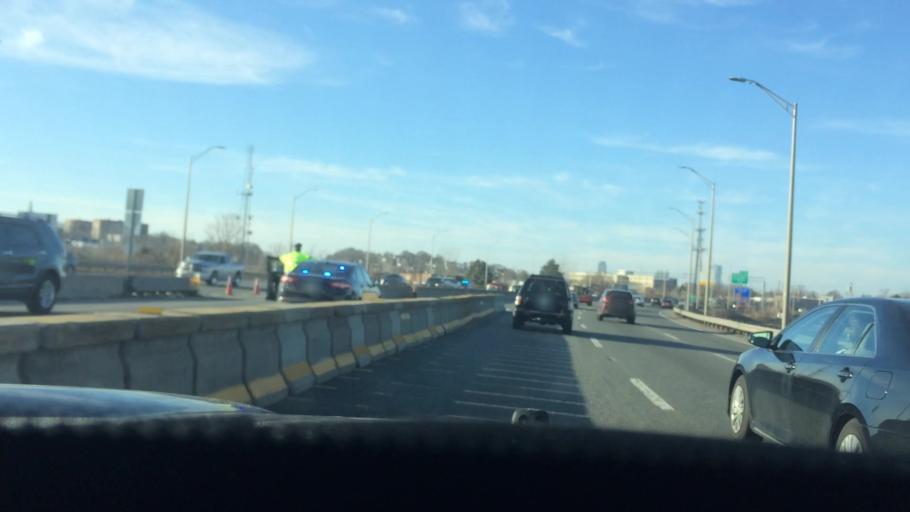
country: US
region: Massachusetts
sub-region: Suffolk County
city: South Boston
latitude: 42.3045
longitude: -71.0524
